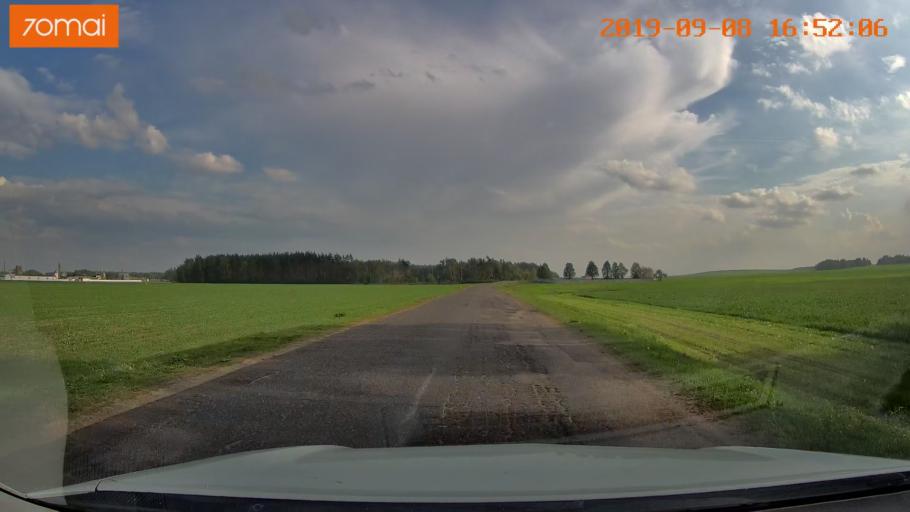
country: BY
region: Grodnenskaya
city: Hrodna
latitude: 53.7783
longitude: 23.9009
